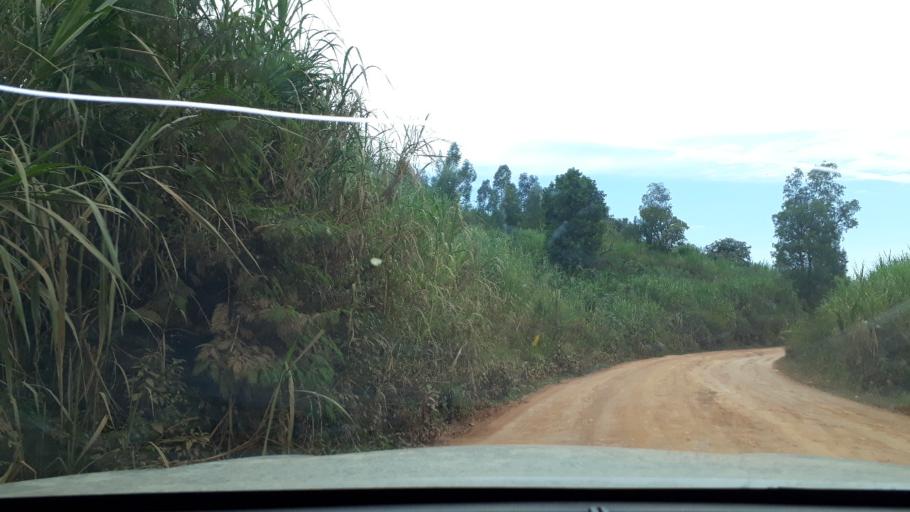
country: CD
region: Eastern Province
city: Bunia
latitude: 1.8198
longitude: 30.4310
